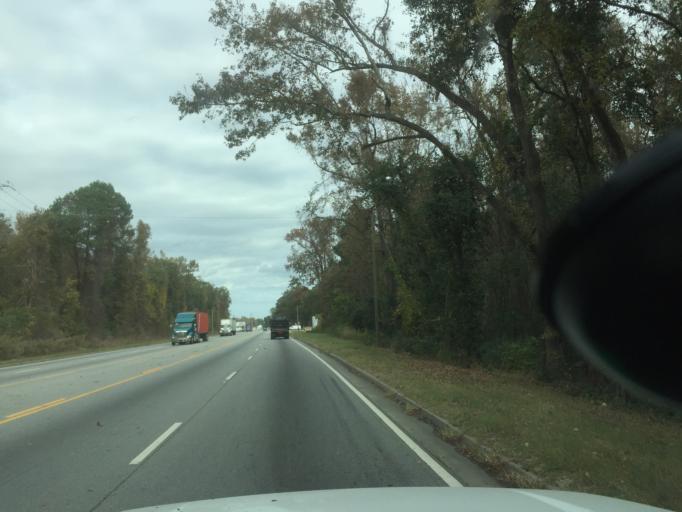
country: US
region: Georgia
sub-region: Chatham County
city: Garden City
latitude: 32.1020
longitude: -81.1958
